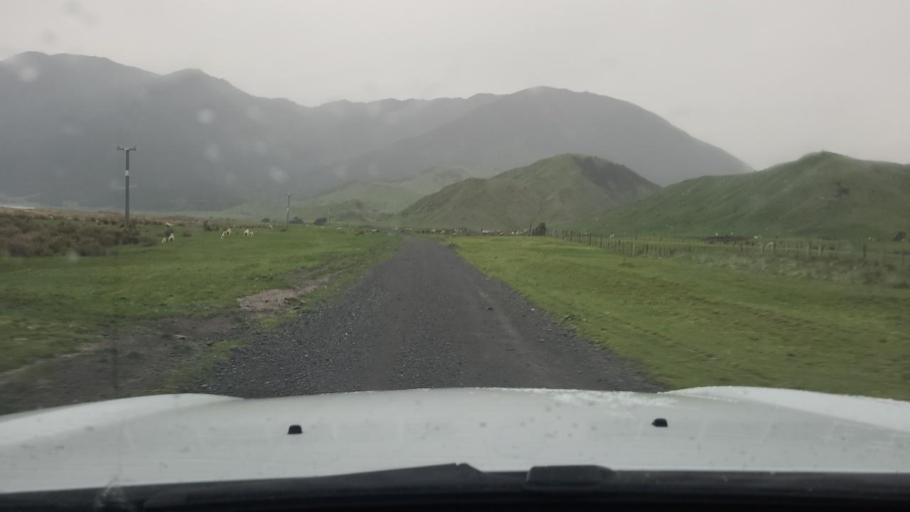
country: NZ
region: Wellington
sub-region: South Wairarapa District
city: Waipawa
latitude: -41.5666
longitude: 175.3901
